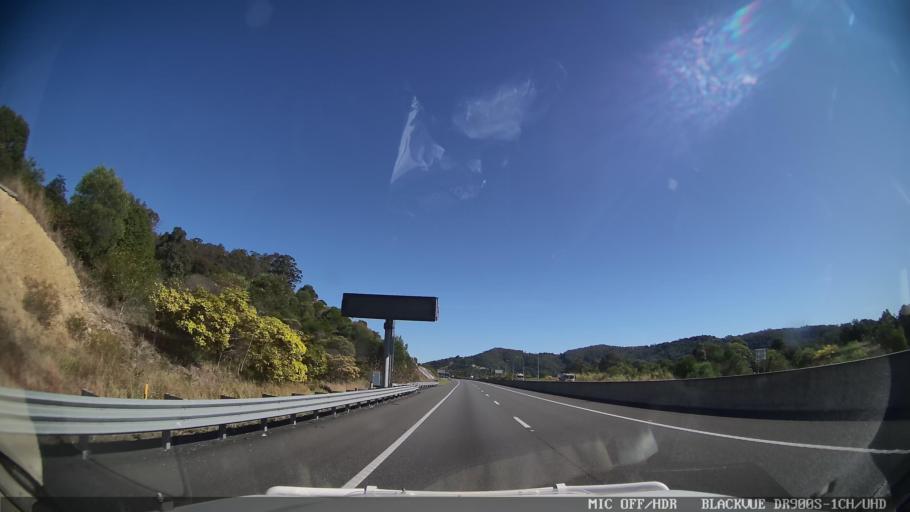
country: AU
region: Queensland
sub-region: Sunshine Coast
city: Black Mountain
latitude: -26.3919
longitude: 152.8114
